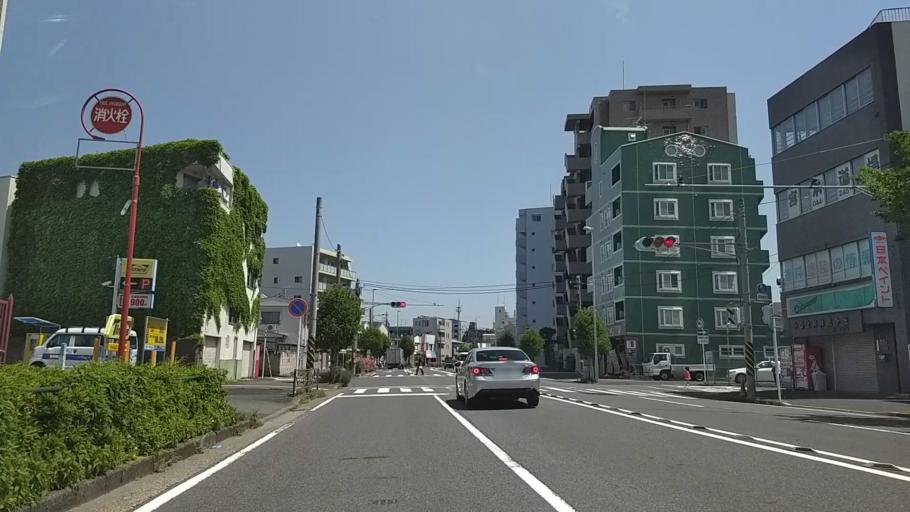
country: JP
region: Kanagawa
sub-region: Kawasaki-shi
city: Kawasaki
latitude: 35.5251
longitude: 139.7097
